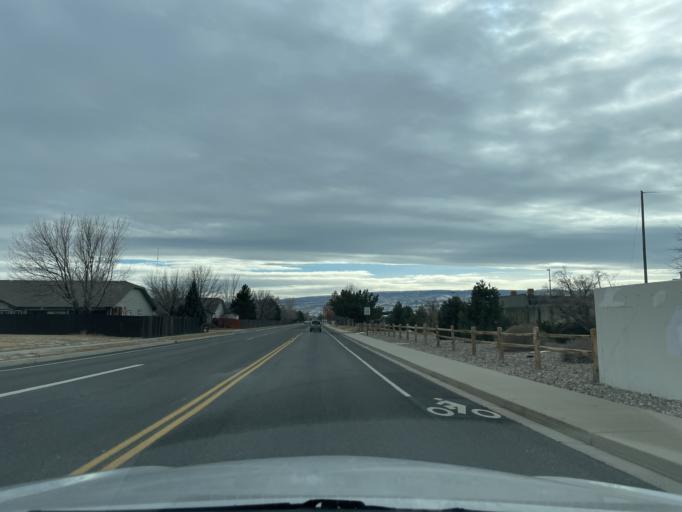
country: US
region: Colorado
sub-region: Mesa County
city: Grand Junction
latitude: 39.0989
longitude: -108.5802
